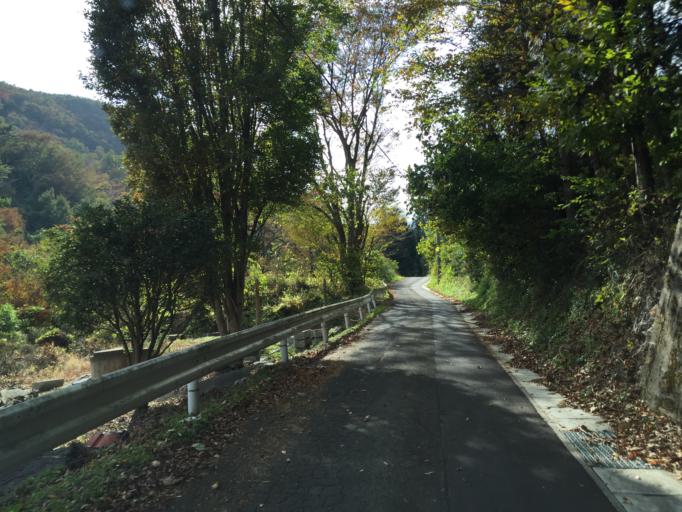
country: JP
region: Fukushima
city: Fukushima-shi
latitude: 37.7384
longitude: 140.3480
